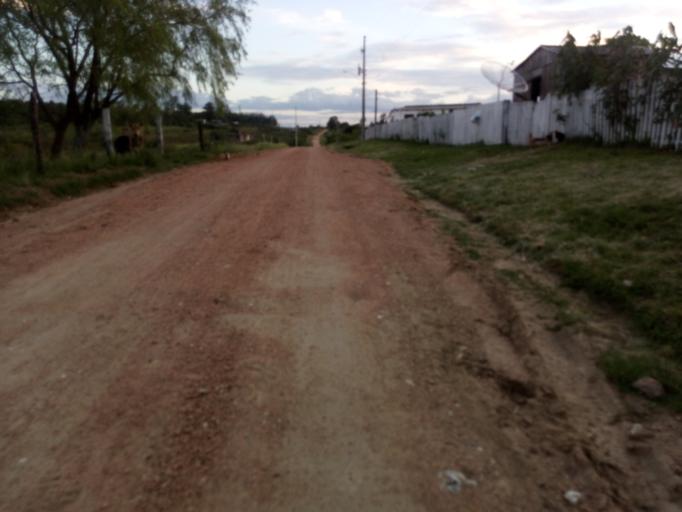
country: BR
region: Rio Grande do Sul
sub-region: Sao Gabriel
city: Sao Gabriel
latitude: -30.3217
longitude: -54.3505
